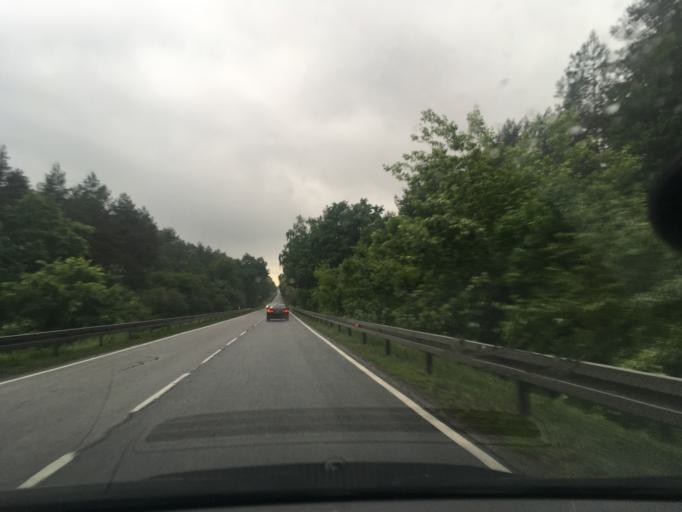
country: PL
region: Lublin Voivodeship
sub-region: Powiat rycki
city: Ryki
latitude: 51.5778
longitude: 21.9073
